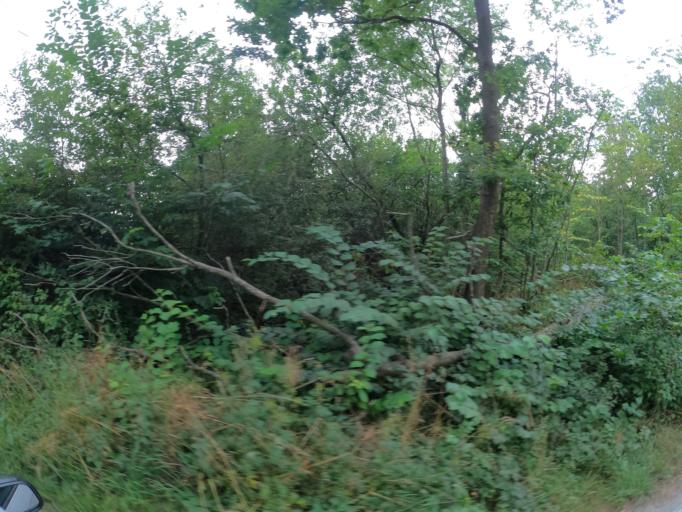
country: SE
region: Skane
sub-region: Lunds Kommun
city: Genarp
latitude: 55.6938
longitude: 13.3283
